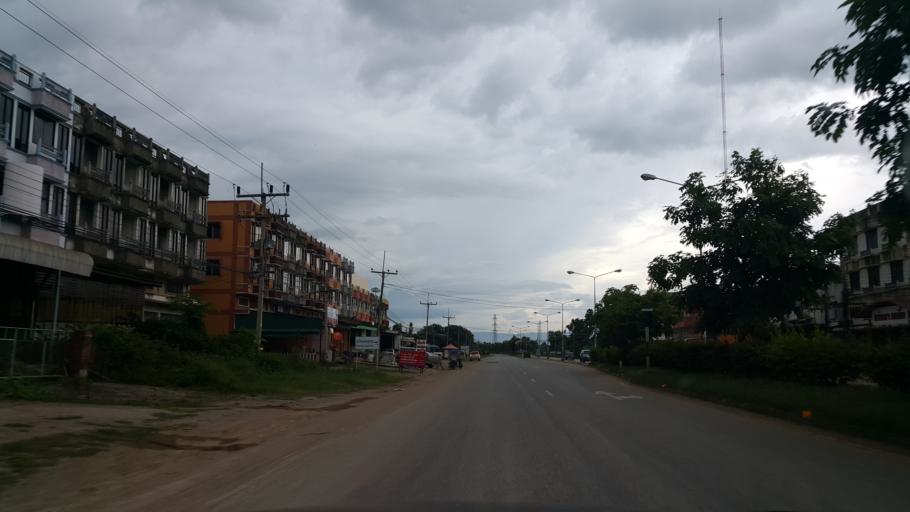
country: TH
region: Phayao
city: Phayao
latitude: 19.1430
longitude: 99.9216
